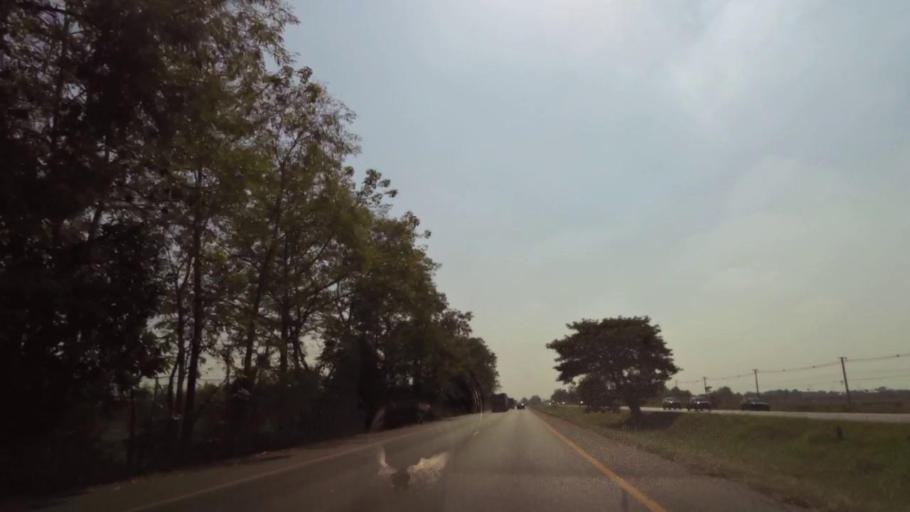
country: TH
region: Phichit
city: Wachira Barami
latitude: 16.4805
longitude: 100.1468
